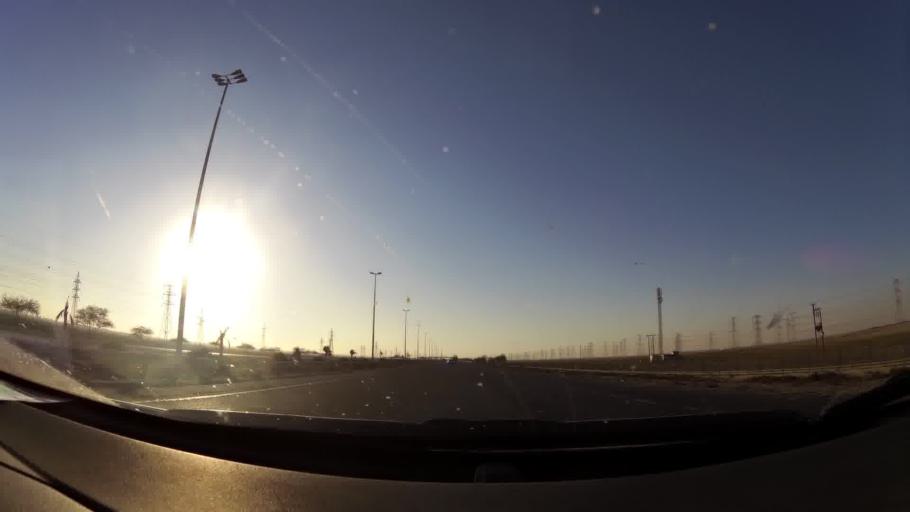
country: KW
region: Al Ahmadi
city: Al Fahahil
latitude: 28.8385
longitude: 48.2505
